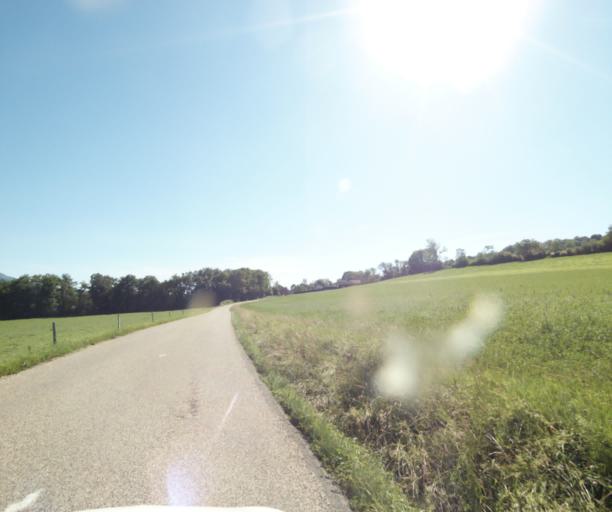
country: FR
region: Rhone-Alpes
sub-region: Departement de la Haute-Savoie
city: Sciez
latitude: 46.3007
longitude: 6.3771
